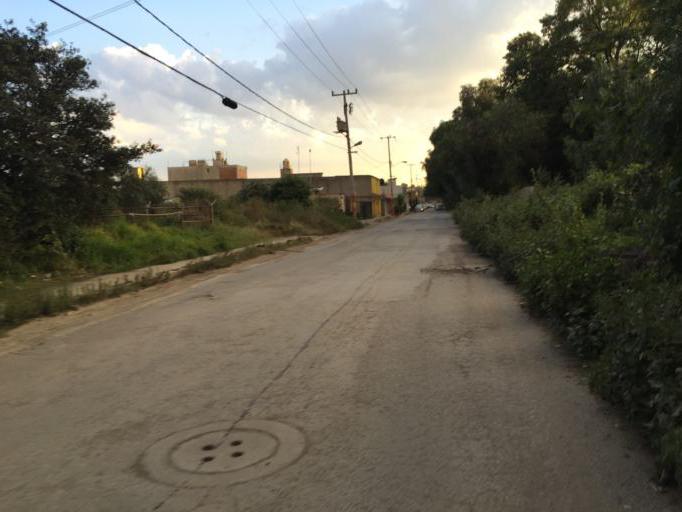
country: MX
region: Mexico
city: Cuautitlan Izcalli
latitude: 19.6649
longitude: -99.2226
